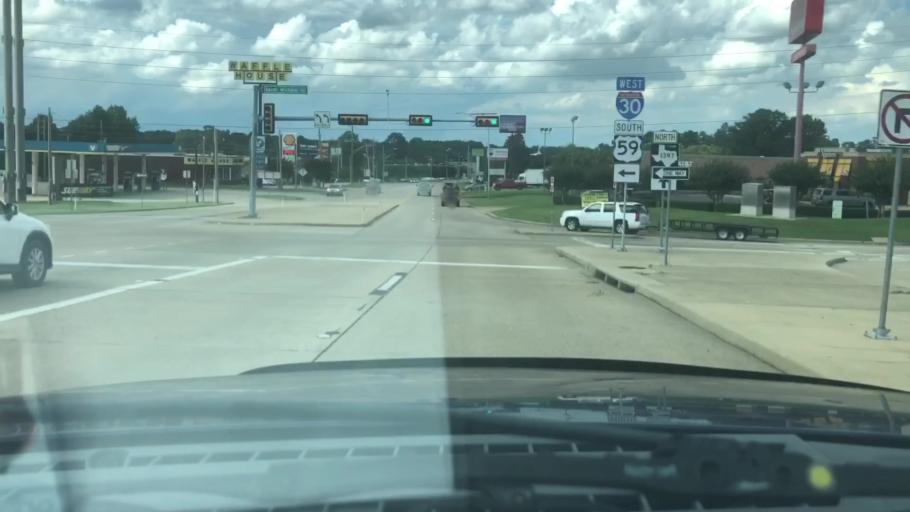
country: US
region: Arkansas
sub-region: Miller County
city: Texarkana
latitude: 33.4666
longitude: -94.0669
